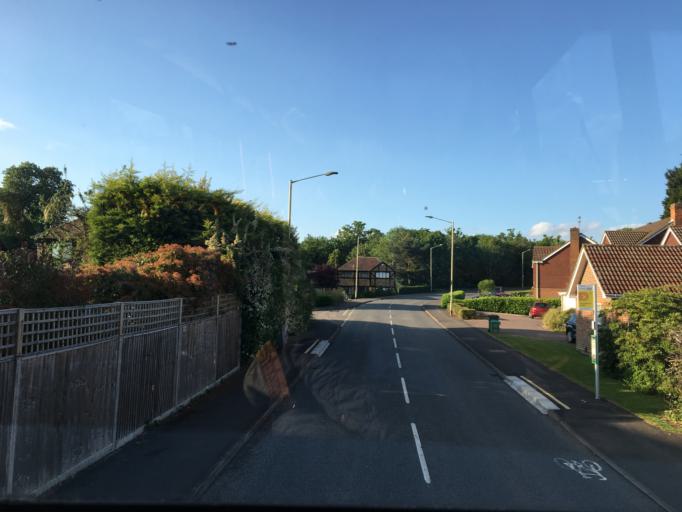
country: GB
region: England
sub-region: West Berkshire
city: Calcot
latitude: 51.4414
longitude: -1.0389
